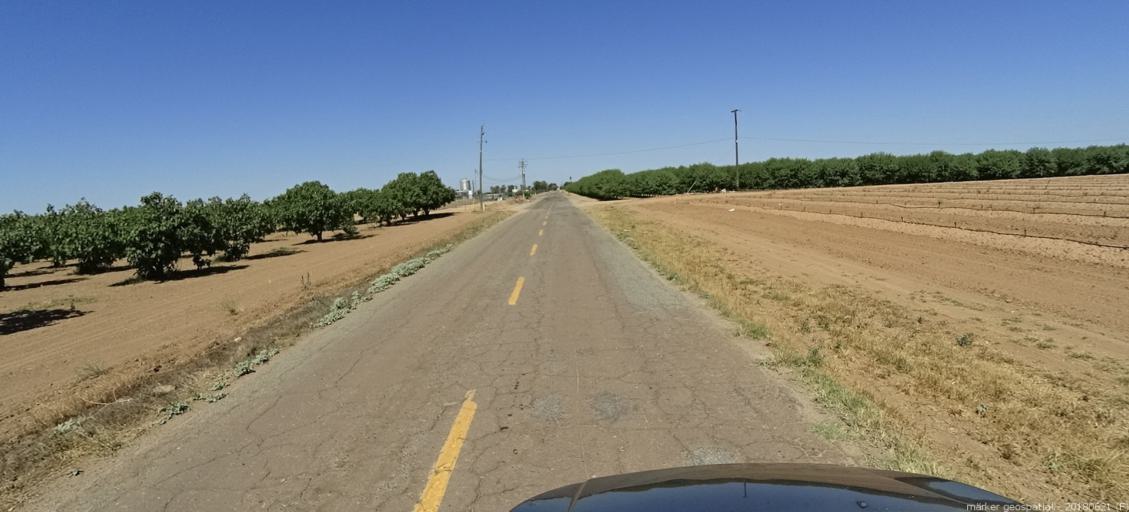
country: US
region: California
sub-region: Madera County
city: Parksdale
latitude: 36.9095
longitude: -119.9463
